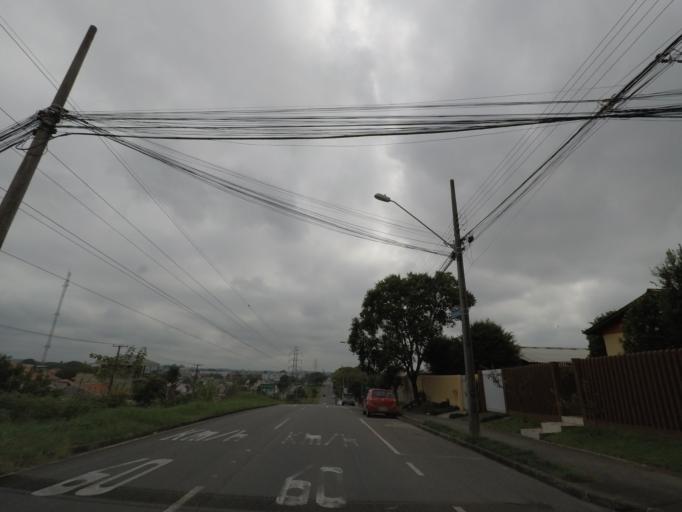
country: BR
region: Parana
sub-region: Curitiba
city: Curitiba
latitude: -25.5023
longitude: -49.3154
